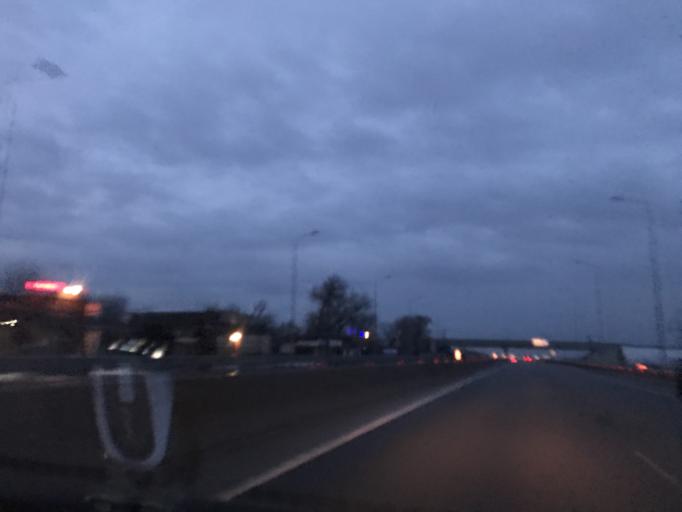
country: RU
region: Rostov
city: Samarskoye
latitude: 46.9393
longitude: 39.7107
